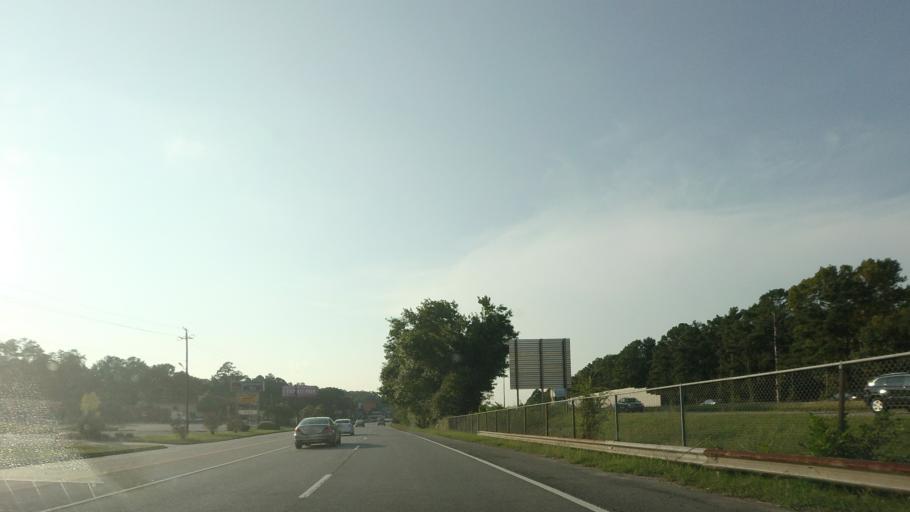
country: US
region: Georgia
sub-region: Bibb County
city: Macon
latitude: 32.8683
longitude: -83.6573
